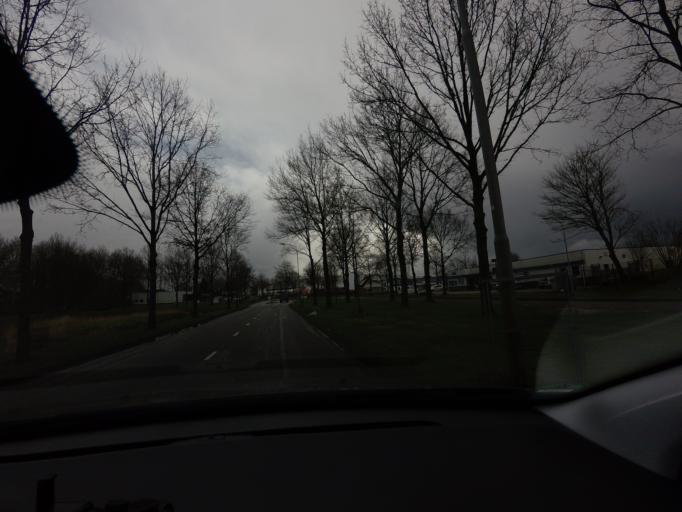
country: NL
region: Drenthe
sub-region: Gemeente Aa en Hunze
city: Anloo
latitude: 52.9991
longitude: 6.7598
